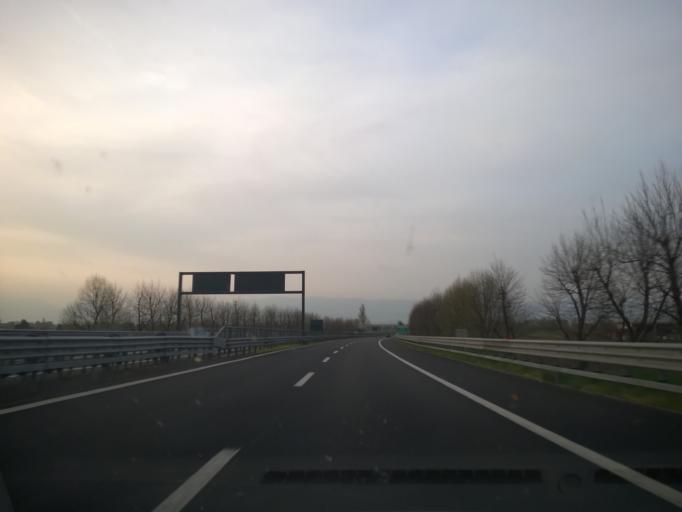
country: IT
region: Veneto
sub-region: Provincia di Vicenza
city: Lisiera
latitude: 45.5838
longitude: 11.5991
